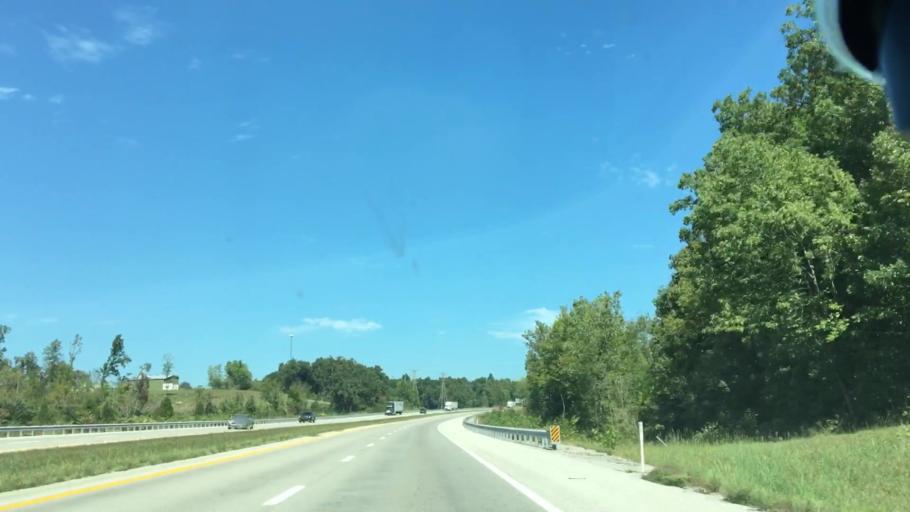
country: US
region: Kentucky
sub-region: Christian County
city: Hopkinsville
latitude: 36.9156
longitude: -87.4741
